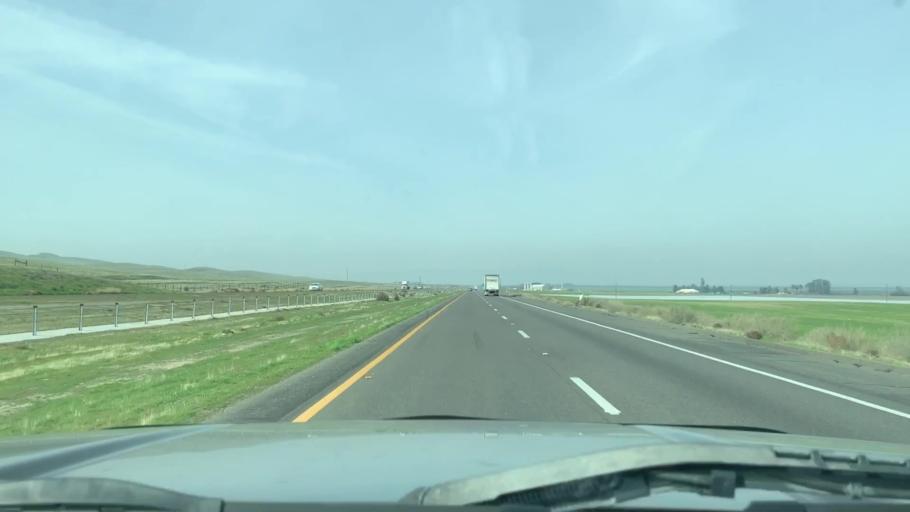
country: US
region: California
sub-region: Kings County
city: Avenal
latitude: 36.0614
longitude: -120.0762
